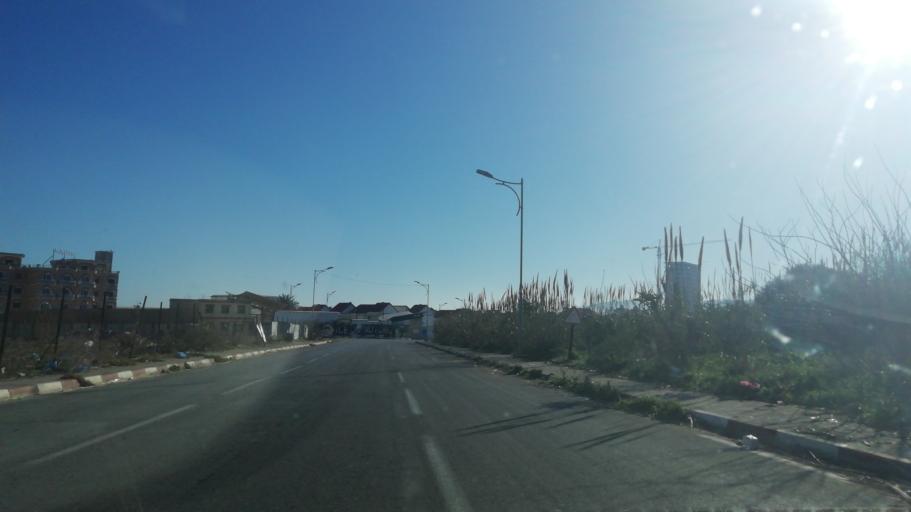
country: DZ
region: Oran
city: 'Ain el Turk
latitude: 35.7581
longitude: -0.7929
